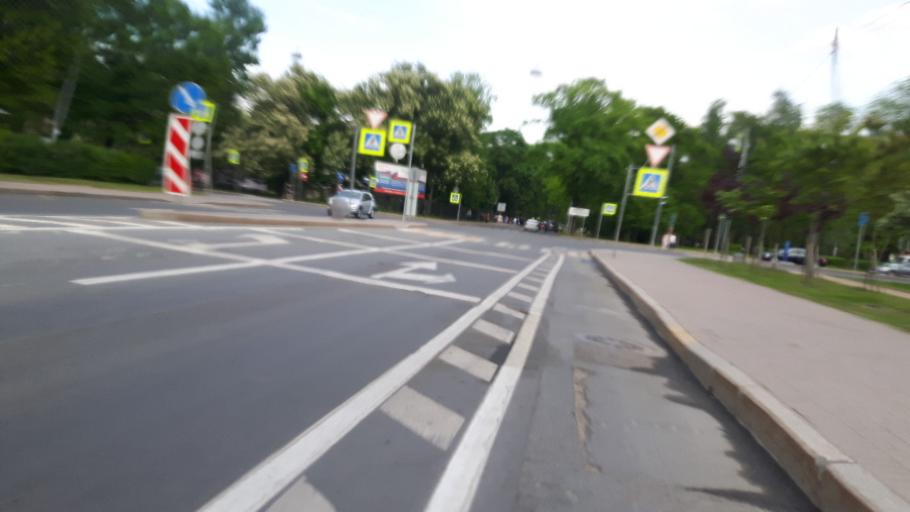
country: RU
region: Leningrad
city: Krestovskiy ostrov
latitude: 59.9706
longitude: 30.2744
